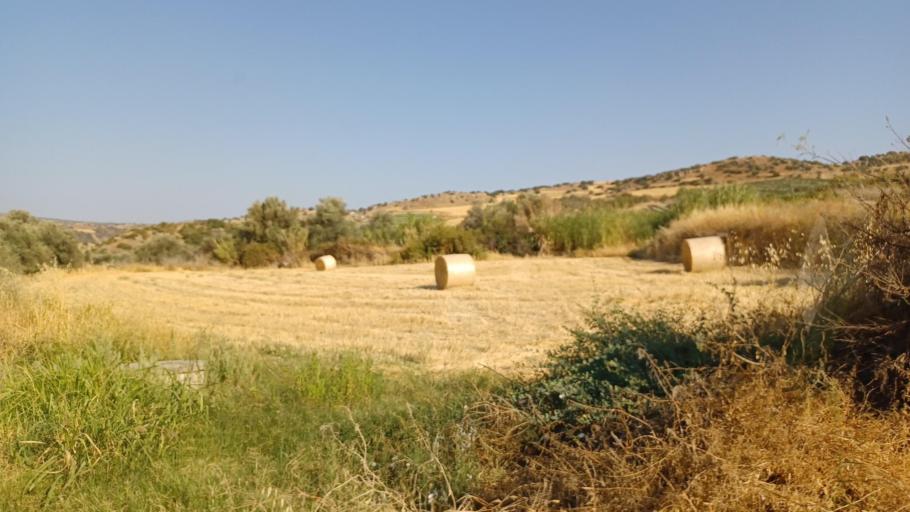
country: CY
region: Pafos
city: Polis
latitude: 34.9569
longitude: 32.4973
